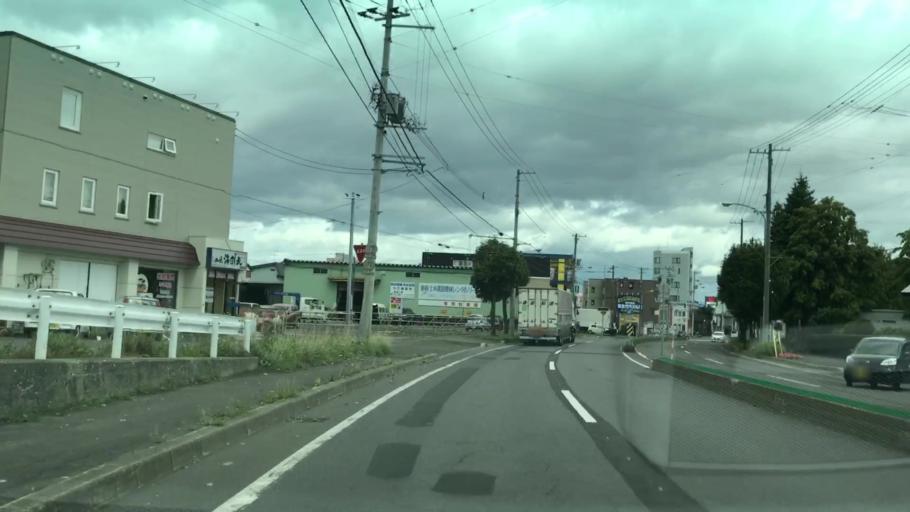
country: JP
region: Hokkaido
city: Sapporo
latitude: 42.9922
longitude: 141.4406
